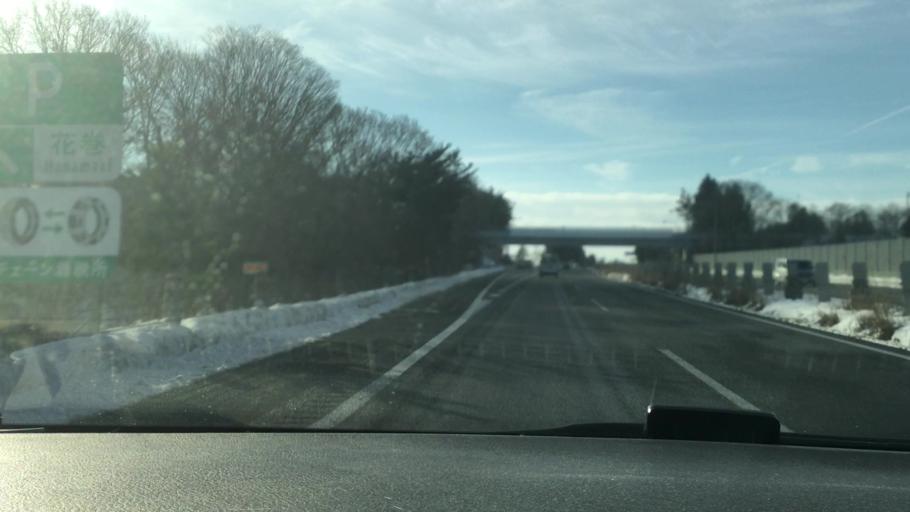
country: JP
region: Iwate
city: Hanamaki
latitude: 39.3726
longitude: 141.0930
